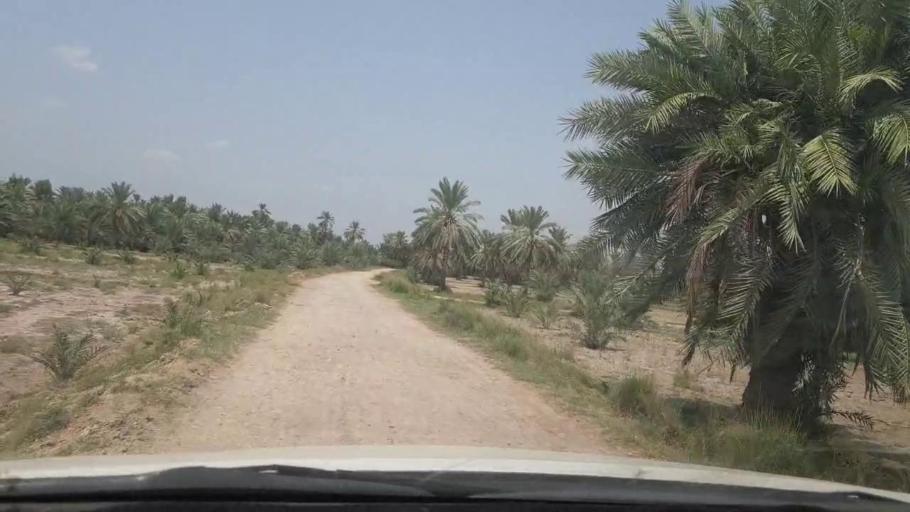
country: PK
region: Sindh
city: Khairpur
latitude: 27.5483
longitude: 68.8280
